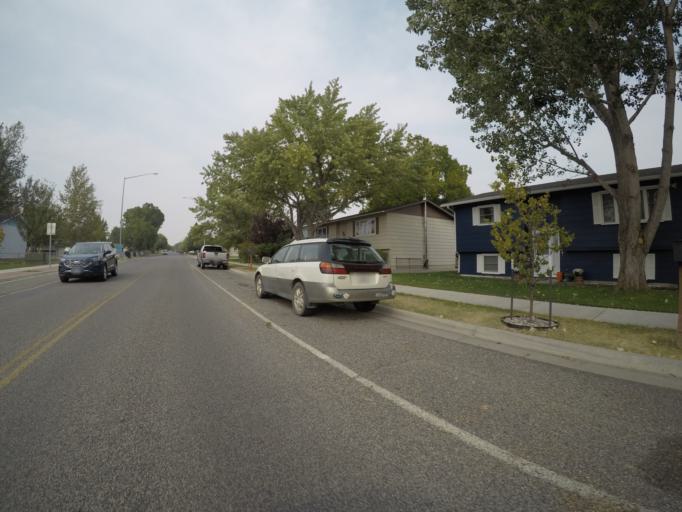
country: US
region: Montana
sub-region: Yellowstone County
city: Laurel
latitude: 45.6770
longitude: -108.7819
